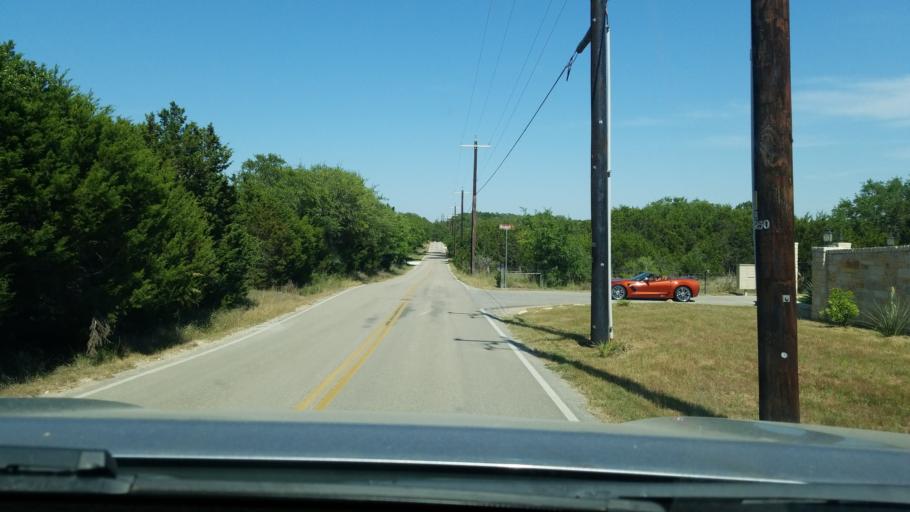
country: US
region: Texas
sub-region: Comal County
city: Bulverde
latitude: 29.7591
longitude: -98.5057
